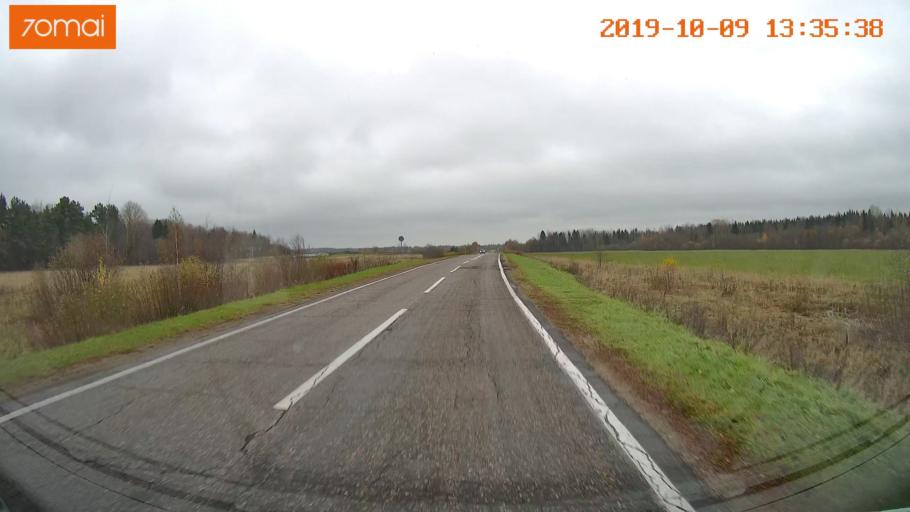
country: RU
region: Jaroslavl
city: Lyubim
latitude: 58.3377
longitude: 41.0813
